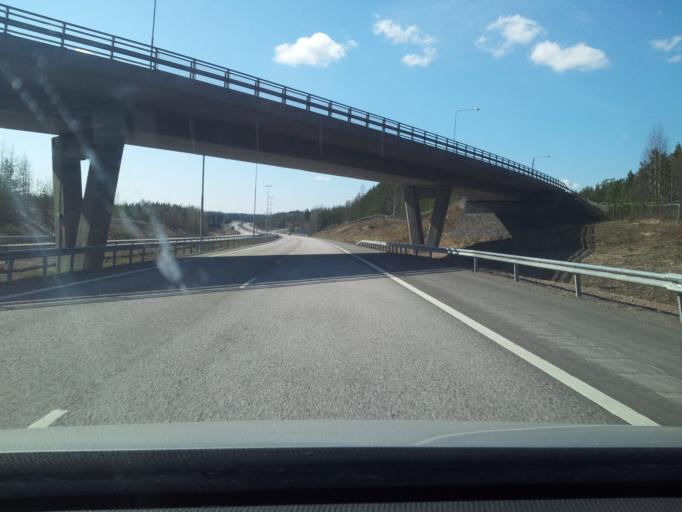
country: FI
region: Uusimaa
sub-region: Loviisa
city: Perna
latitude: 60.4915
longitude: 25.9807
